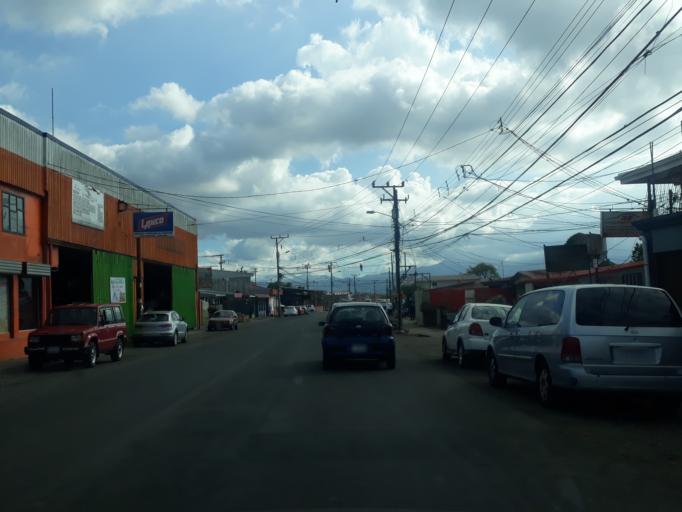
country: CR
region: San Jose
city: Ipis
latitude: 9.9865
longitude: -84.0266
